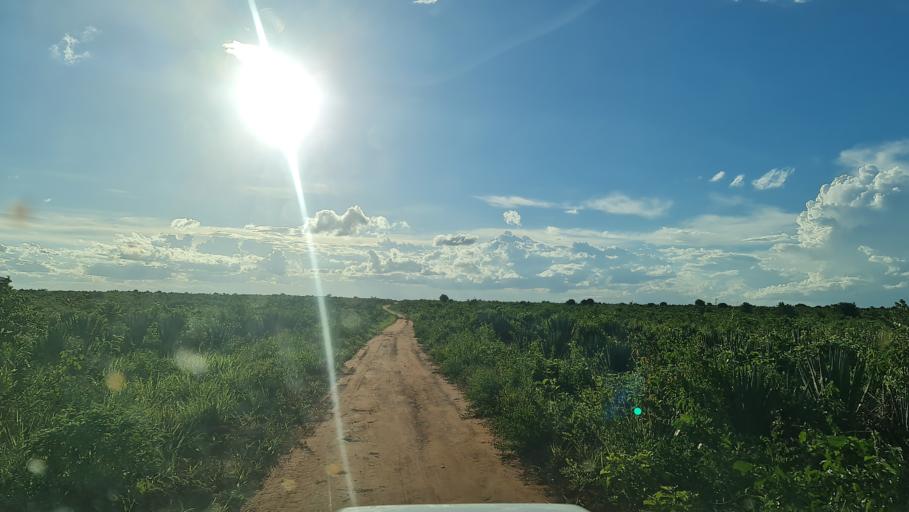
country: MZ
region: Nampula
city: Ilha de Mocambique
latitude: -14.9521
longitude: 40.1778
